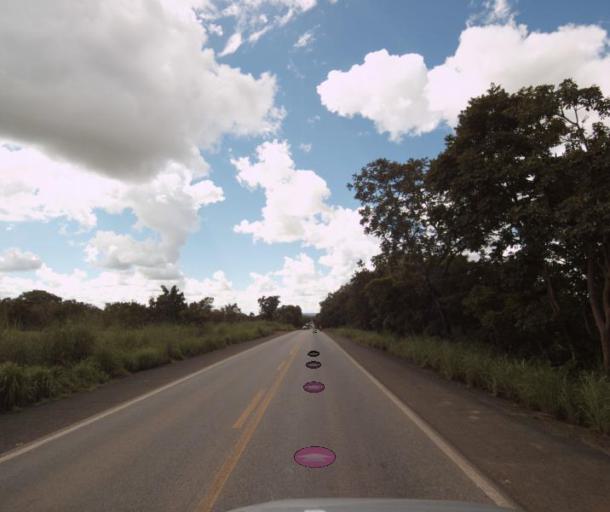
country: BR
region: Goias
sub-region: Porangatu
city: Porangatu
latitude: -13.7824
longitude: -49.0329
